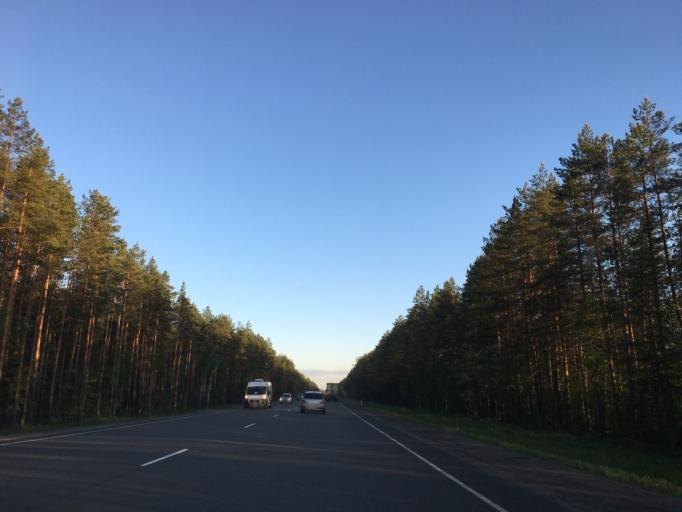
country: RU
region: Leningrad
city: Rozhdestveno
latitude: 59.2946
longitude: 29.9404
